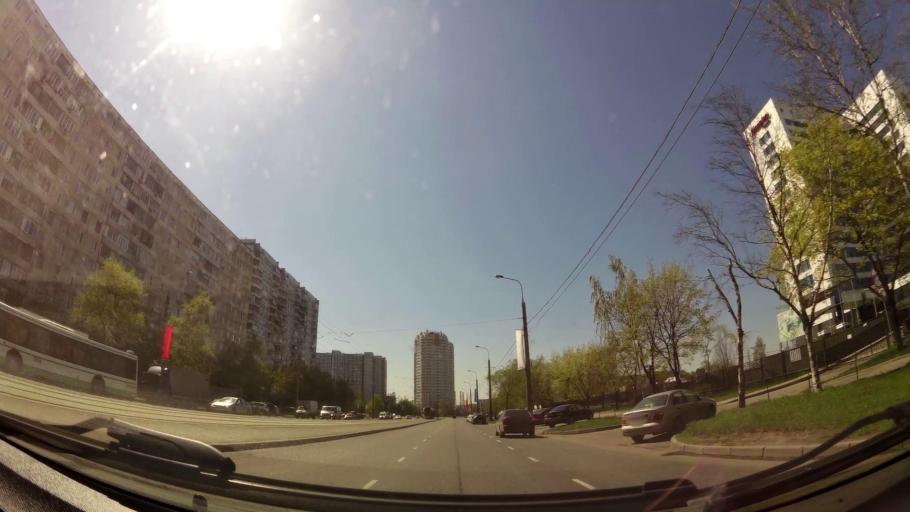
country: RU
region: Moscow
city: Strogino
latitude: 55.8027
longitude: 37.3919
